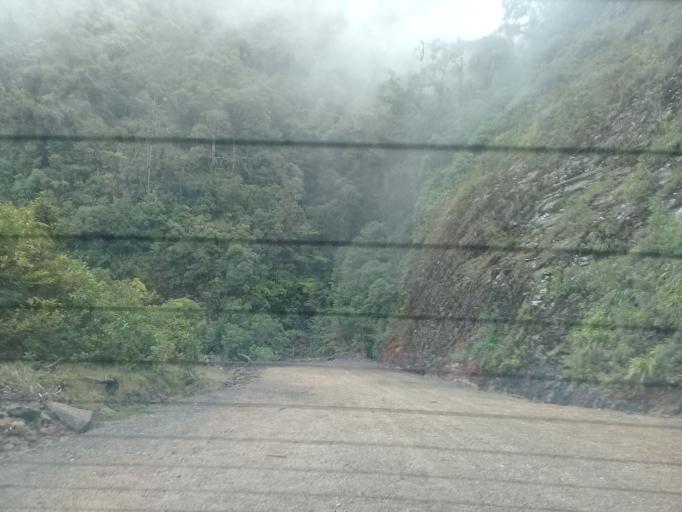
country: CO
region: Cundinamarca
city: Gachala
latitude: 4.6987
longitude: -73.4113
